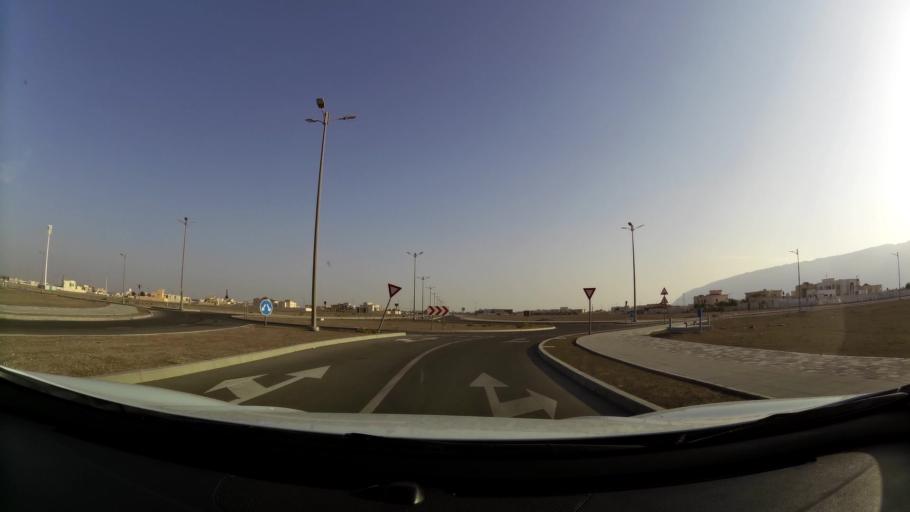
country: AE
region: Abu Dhabi
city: Al Ain
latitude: 24.1022
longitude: 55.8414
